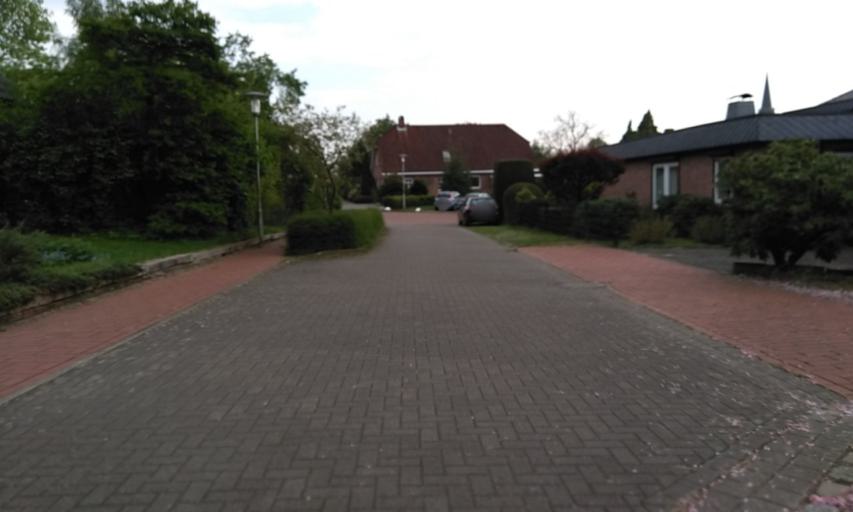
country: DE
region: Lower Saxony
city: Harsefeld
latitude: 53.4563
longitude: 9.5050
